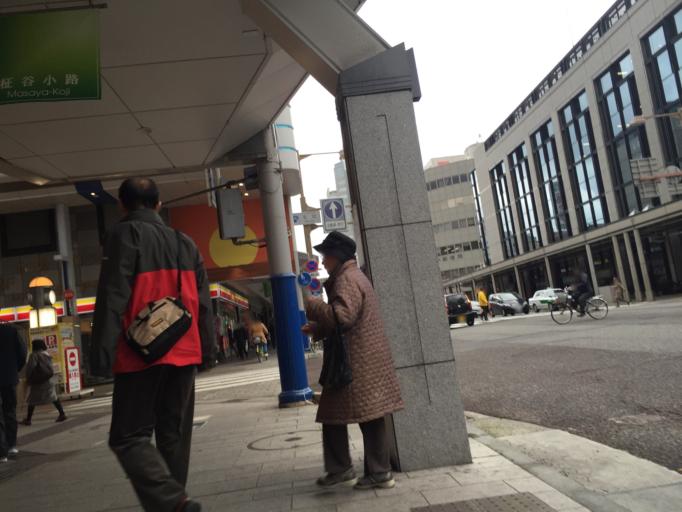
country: JP
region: Niigata
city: Niigata-shi
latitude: 37.9215
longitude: 139.0472
